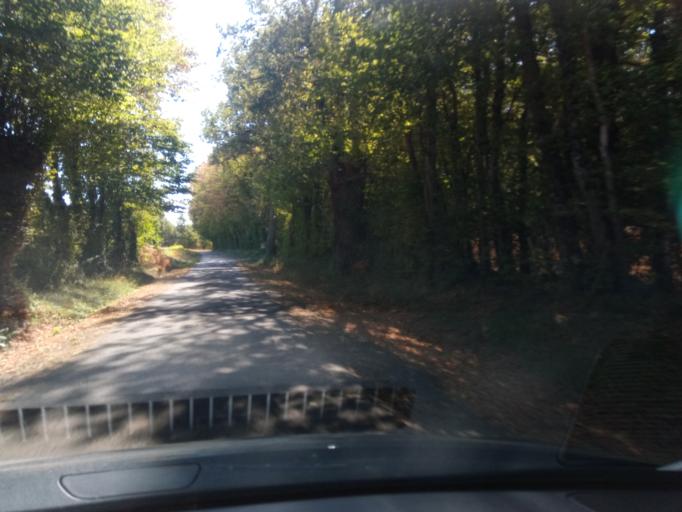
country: FR
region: Poitou-Charentes
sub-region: Departement de la Vienne
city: Lussac-les-Chateaux
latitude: 46.3870
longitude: 0.7668
